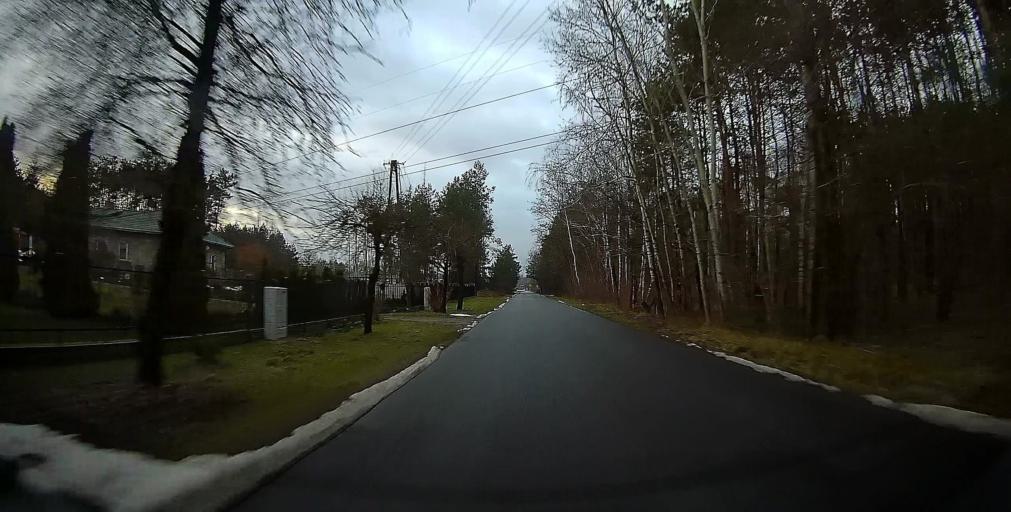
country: PL
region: Masovian Voivodeship
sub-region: Radom
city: Radom
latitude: 51.4524
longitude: 21.1298
